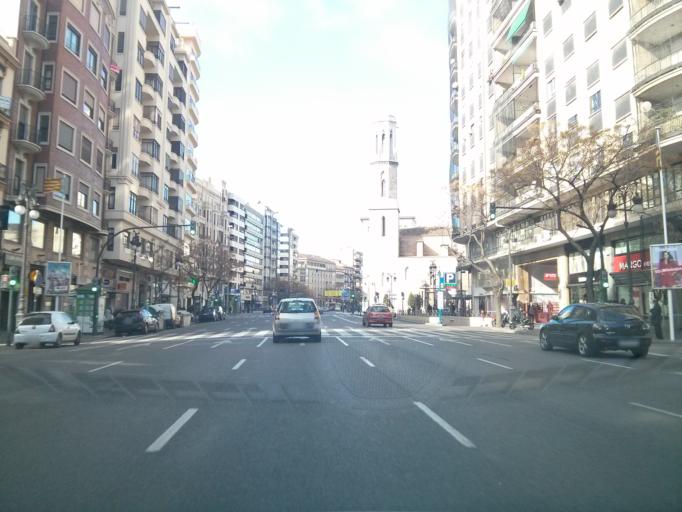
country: ES
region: Valencia
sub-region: Provincia de Valencia
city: Valencia
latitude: 39.4679
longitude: -0.3786
